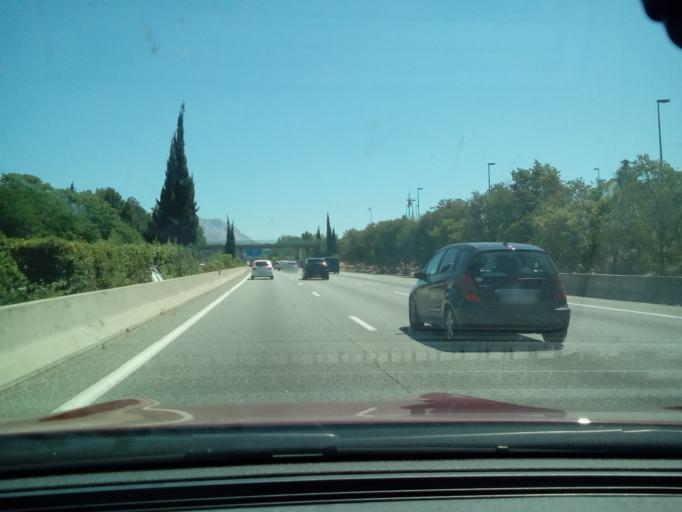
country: FR
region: Provence-Alpes-Cote d'Azur
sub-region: Departement des Bouches-du-Rhone
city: Aix-en-Provence
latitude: 43.5122
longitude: 5.4614
